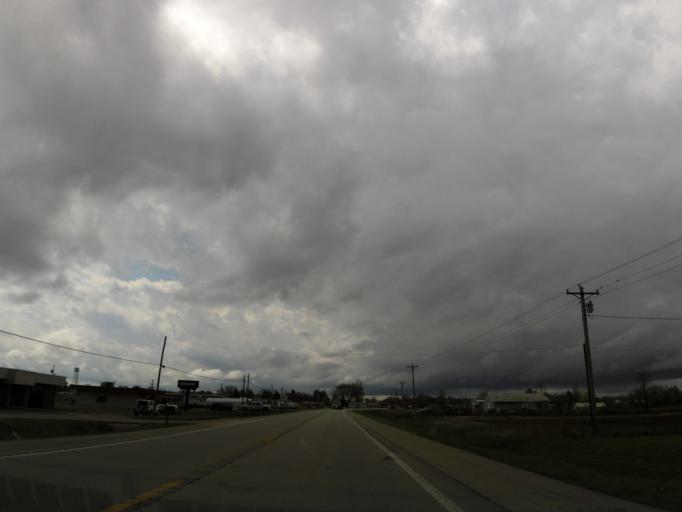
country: US
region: Arkansas
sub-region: Clay County
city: Corning
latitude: 36.5520
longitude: -90.5212
